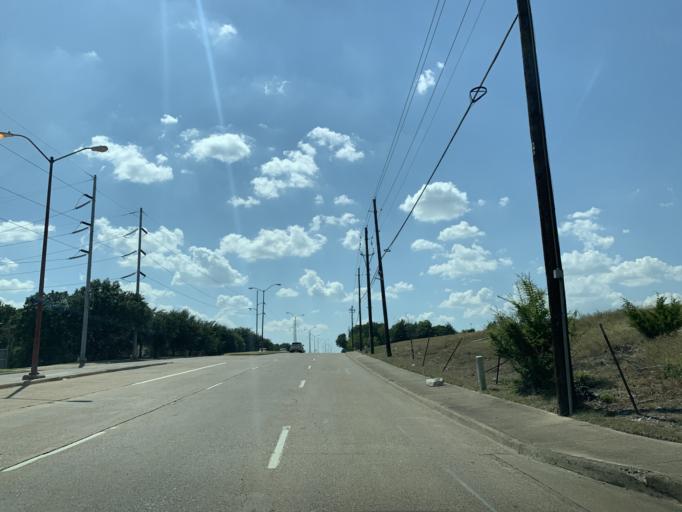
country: US
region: Texas
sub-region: Dallas County
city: DeSoto
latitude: 32.6625
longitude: -96.8149
